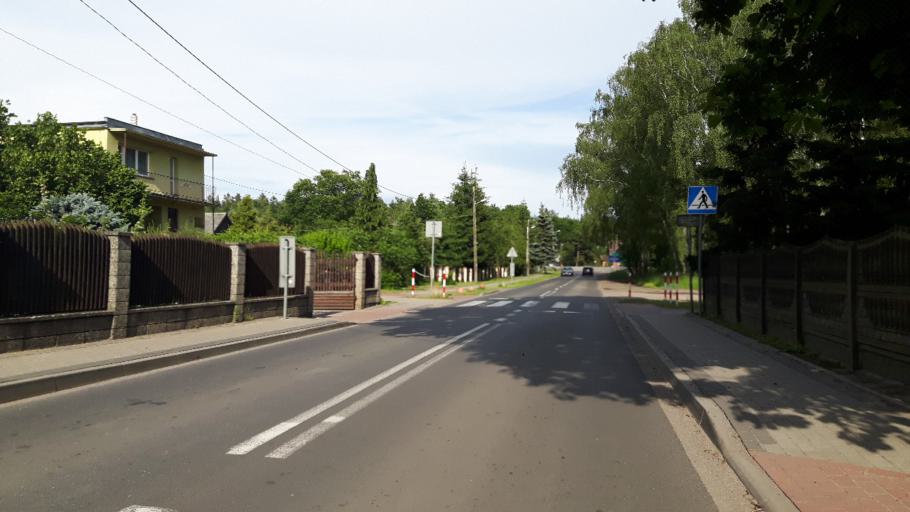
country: PL
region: West Pomeranian Voivodeship
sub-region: Powiat goleniowski
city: Goleniow
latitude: 53.4616
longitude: 14.7851
